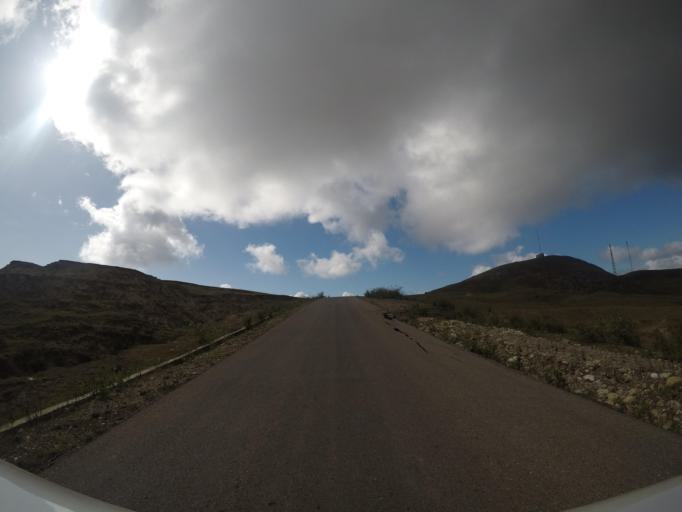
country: TL
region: Lautem
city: Lospalos
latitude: -8.4771
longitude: 126.8690
